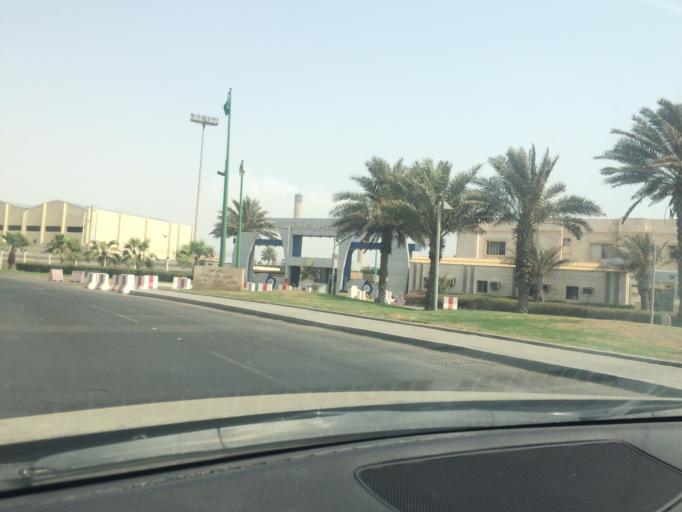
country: SA
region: Makkah
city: Jeddah
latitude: 21.5589
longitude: 39.1122
